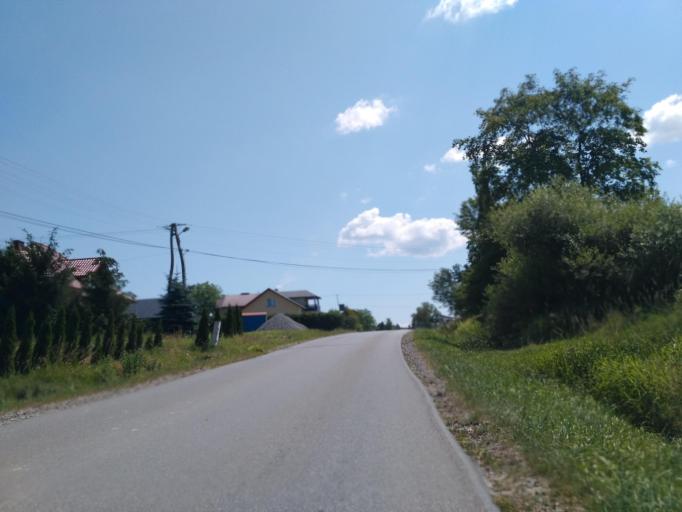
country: PL
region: Subcarpathian Voivodeship
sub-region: Powiat sanocki
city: Niebieszczany
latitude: 49.4933
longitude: 22.1729
